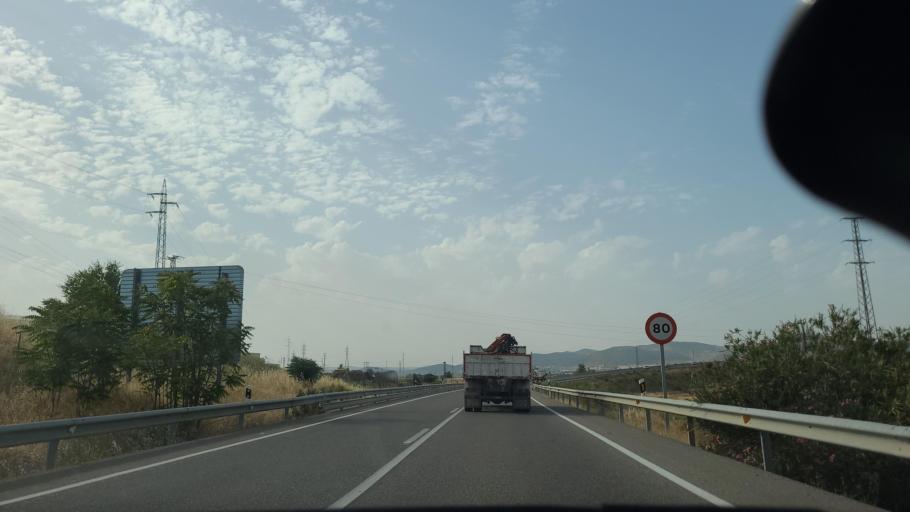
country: ES
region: Andalusia
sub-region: Province of Cordoba
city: Penarroya-Pueblonuevo
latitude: 38.2991
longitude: -5.2798
